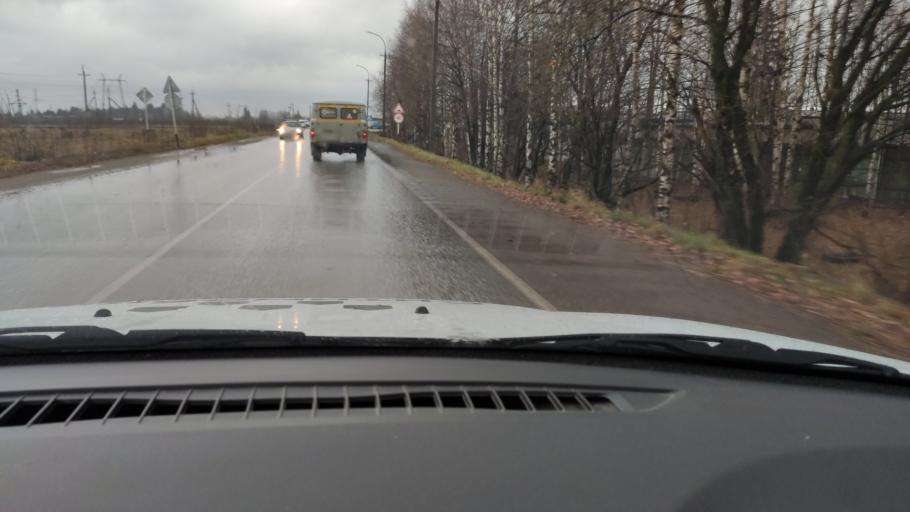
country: RU
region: Perm
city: Sylva
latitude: 58.0278
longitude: 56.7163
